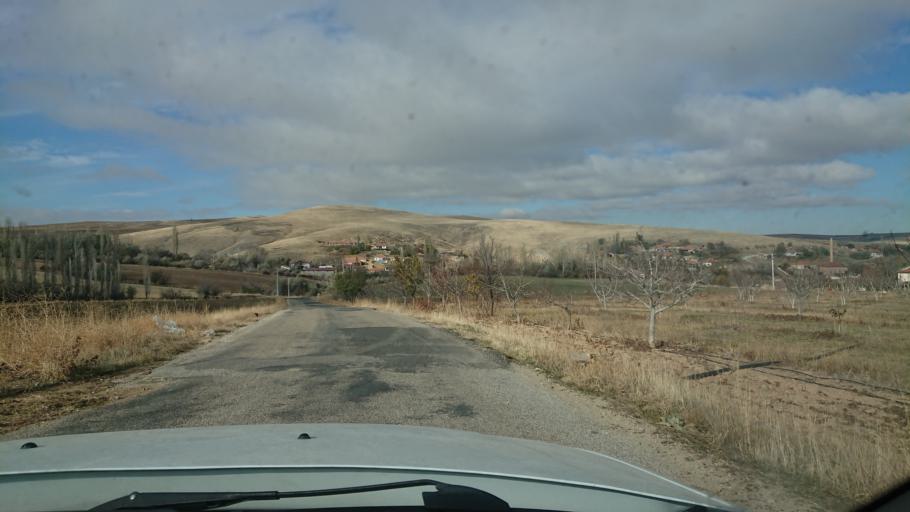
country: TR
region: Aksaray
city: Ortakoy
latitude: 38.8033
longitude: 33.9869
